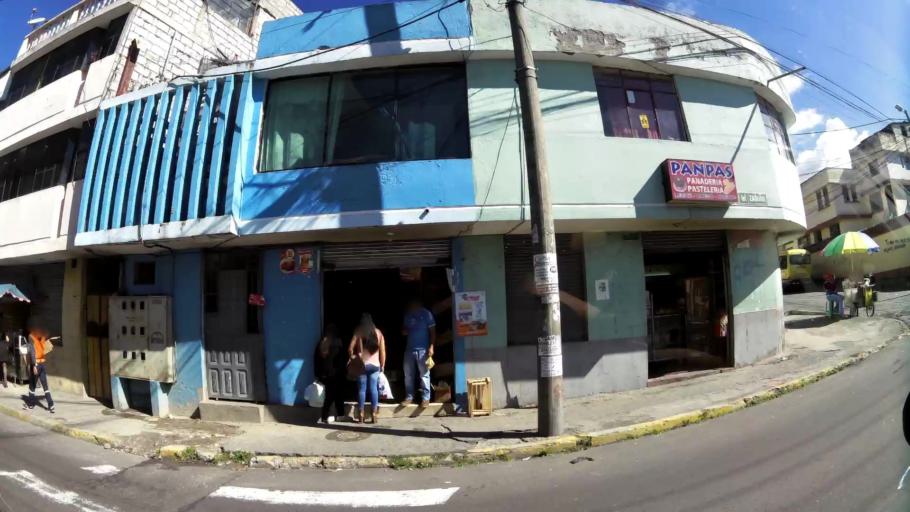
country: EC
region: Pichincha
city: Quito
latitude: -0.2378
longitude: -78.5335
